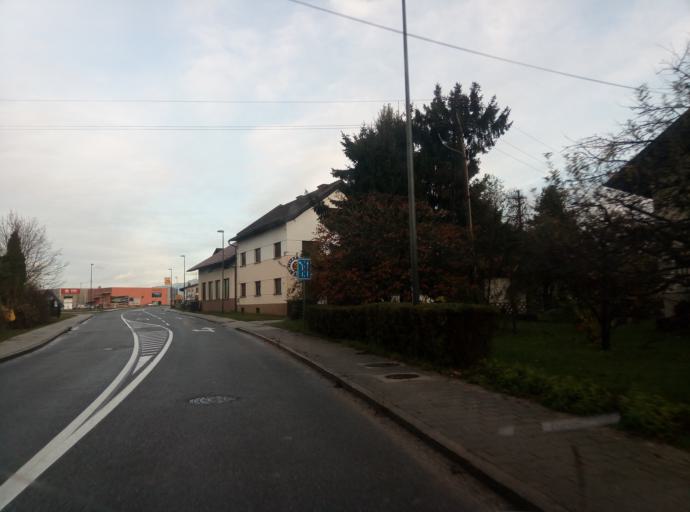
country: SI
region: Menges
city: Menges
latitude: 46.1732
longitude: 14.5695
